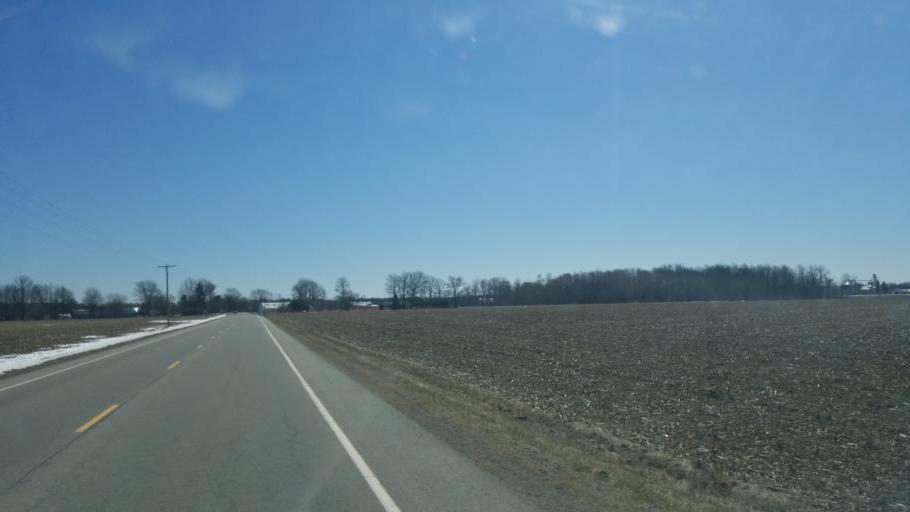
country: US
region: Ohio
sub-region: Crawford County
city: Galion
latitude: 40.8095
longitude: -82.8278
